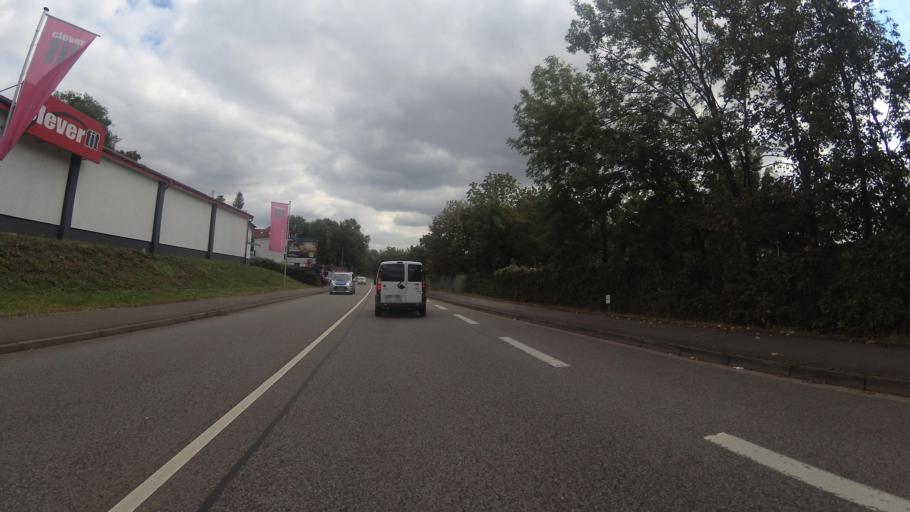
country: DE
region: Saarland
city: Volklingen
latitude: 49.2638
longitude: 6.8369
